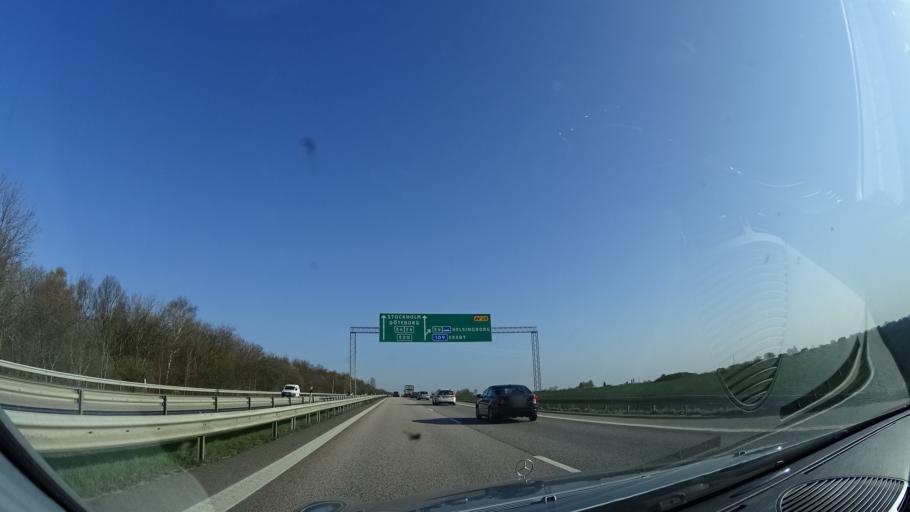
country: SE
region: Skane
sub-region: Helsingborg
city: Gantofta
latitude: 56.0044
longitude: 12.7799
